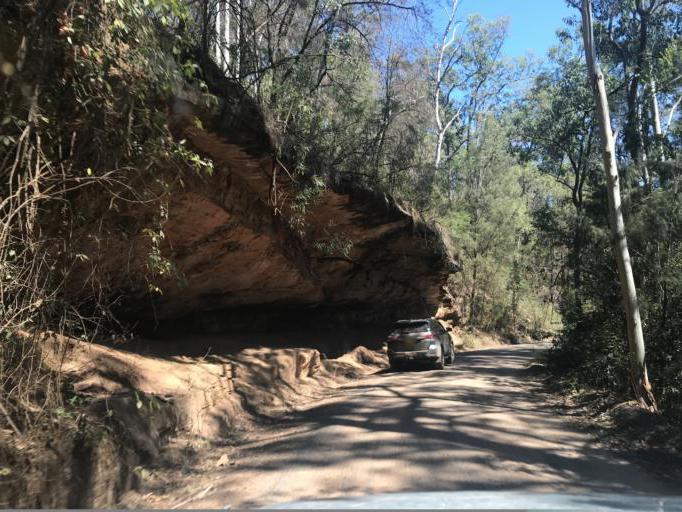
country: AU
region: New South Wales
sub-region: Wyong Shire
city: Little Jilliby
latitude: -33.1798
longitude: 151.0649
